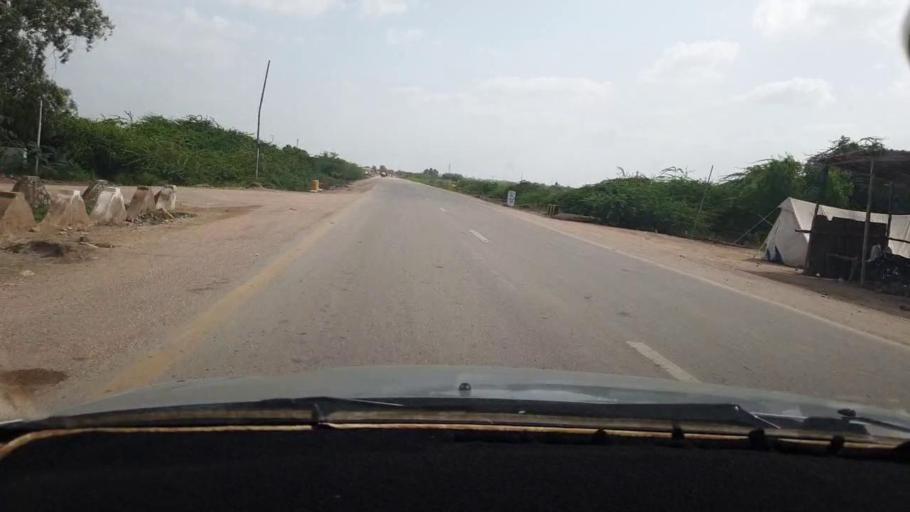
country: PK
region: Sindh
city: Naukot
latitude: 24.9866
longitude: 69.2926
